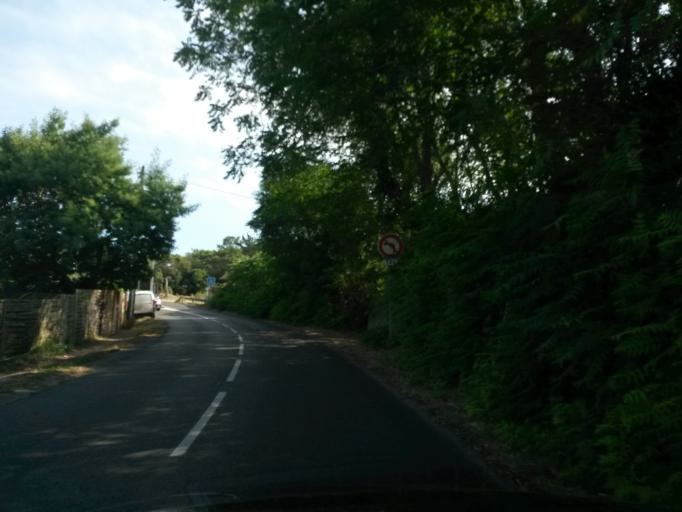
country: FR
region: Pays de la Loire
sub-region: Departement de la Vendee
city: Les Sables-d'Olonne
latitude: 46.5248
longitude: -1.8104
